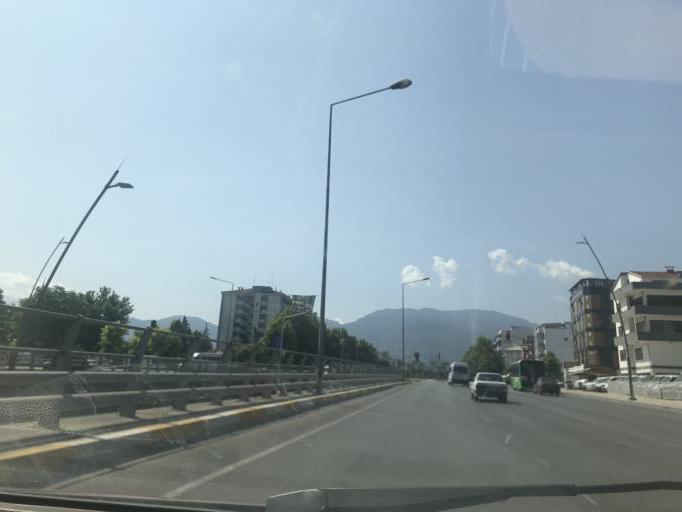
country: TR
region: Denizli
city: Denizli
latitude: 37.7795
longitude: 29.0975
